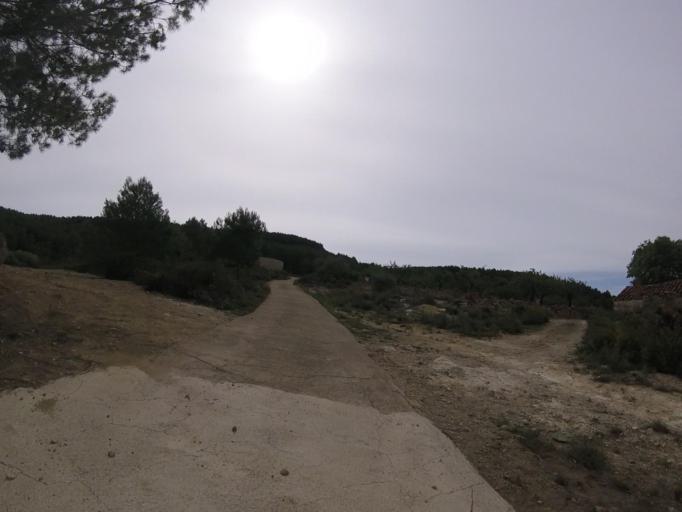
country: ES
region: Valencia
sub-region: Provincia de Castello
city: Cabanes
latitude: 40.1921
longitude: 0.0765
